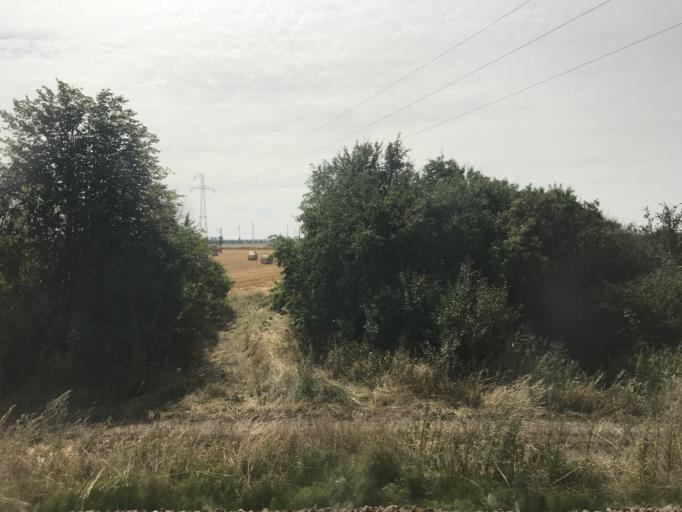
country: PL
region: Kujawsko-Pomorskie
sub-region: Powiat inowroclawski
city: Inowroclaw
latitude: 52.7883
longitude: 18.2065
